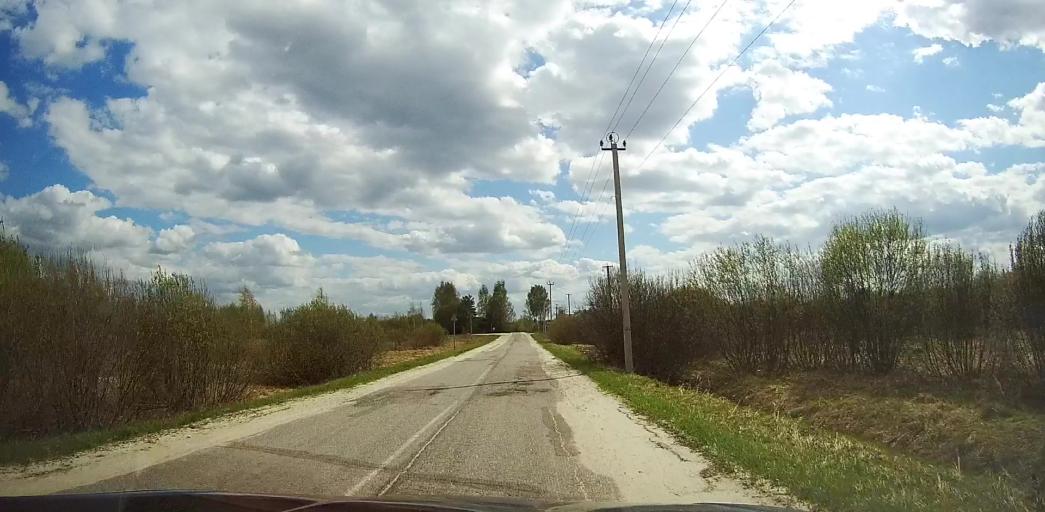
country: RU
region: Moskovskaya
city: Davydovo
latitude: 55.6338
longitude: 38.7830
